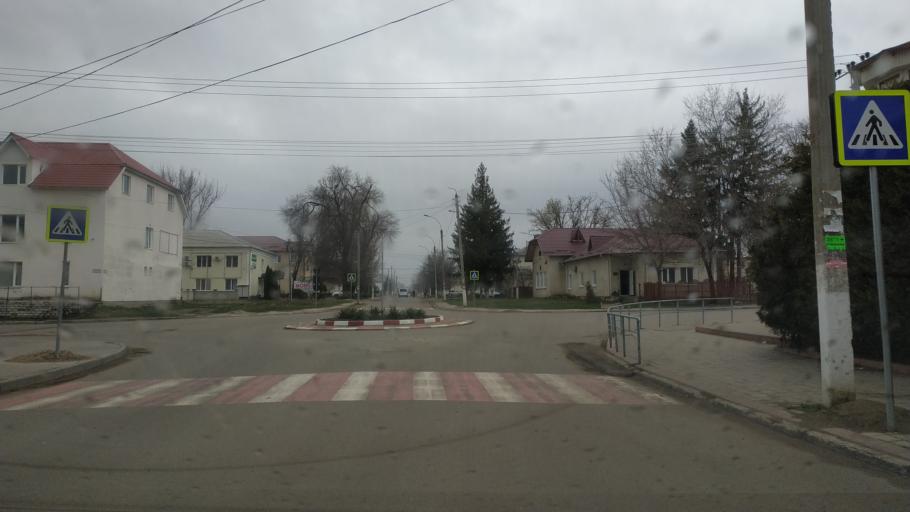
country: MD
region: Leova
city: Leova
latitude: 46.4831
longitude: 28.2516
